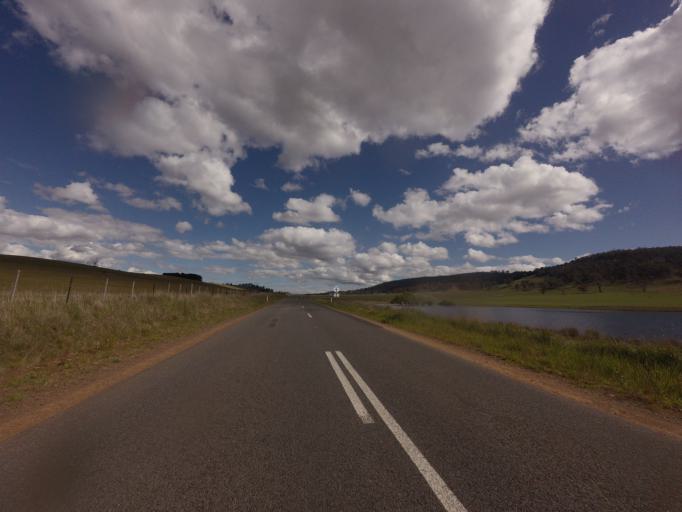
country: AU
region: Tasmania
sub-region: Brighton
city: Bridgewater
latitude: -42.4195
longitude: 147.3111
